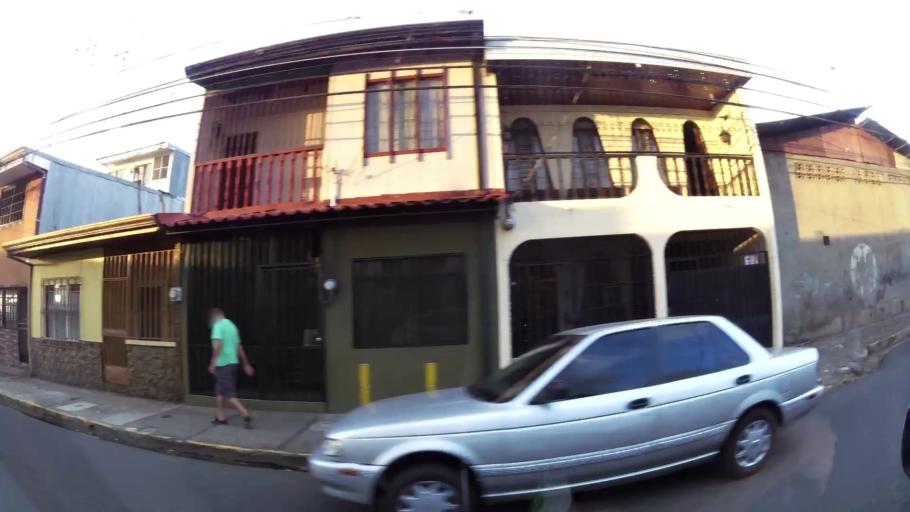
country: CR
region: Heredia
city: Heredia
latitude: 9.9932
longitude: -84.1189
